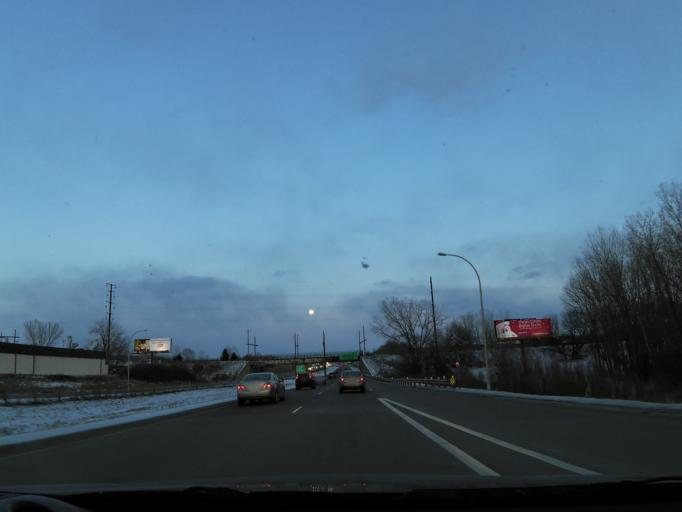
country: US
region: Minnesota
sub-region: Ramsey County
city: Vadnais Heights
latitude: 45.0373
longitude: -93.0386
